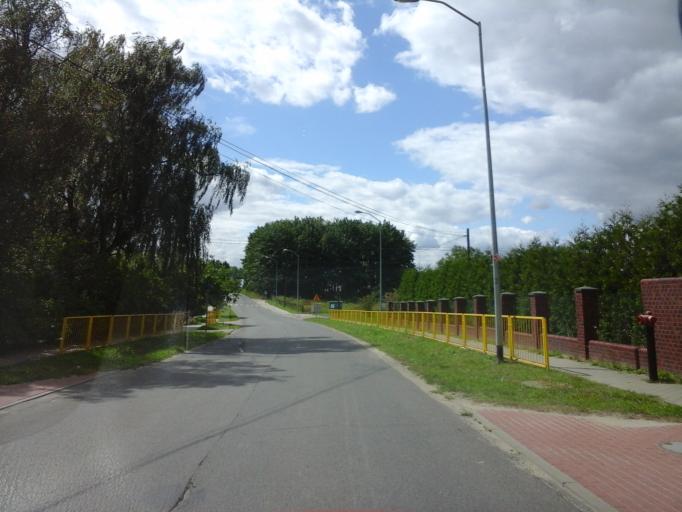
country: PL
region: West Pomeranian Voivodeship
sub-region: Powiat policki
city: Przeclaw
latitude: 53.4241
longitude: 14.4505
